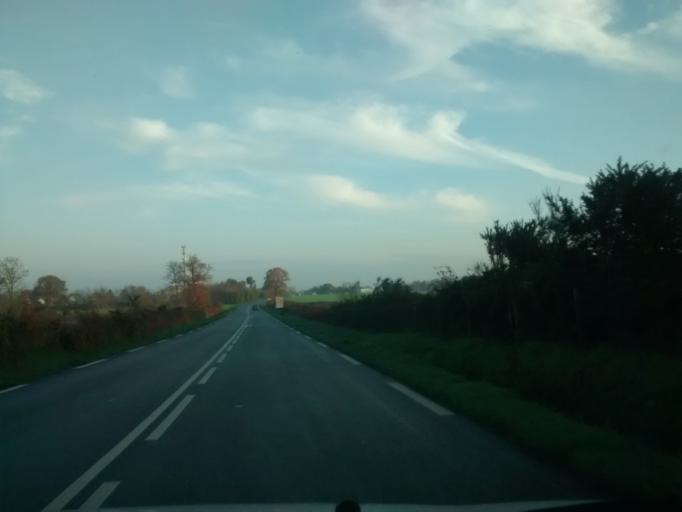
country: FR
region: Brittany
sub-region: Departement d'Ille-et-Vilaine
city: Sens-de-Bretagne
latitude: 48.3237
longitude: -1.5292
